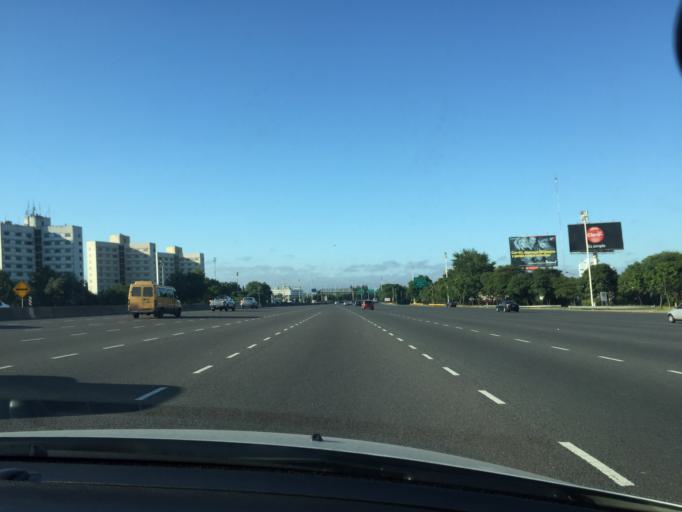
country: AR
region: Buenos Aires F.D.
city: Villa Lugano
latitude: -34.6995
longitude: -58.4967
